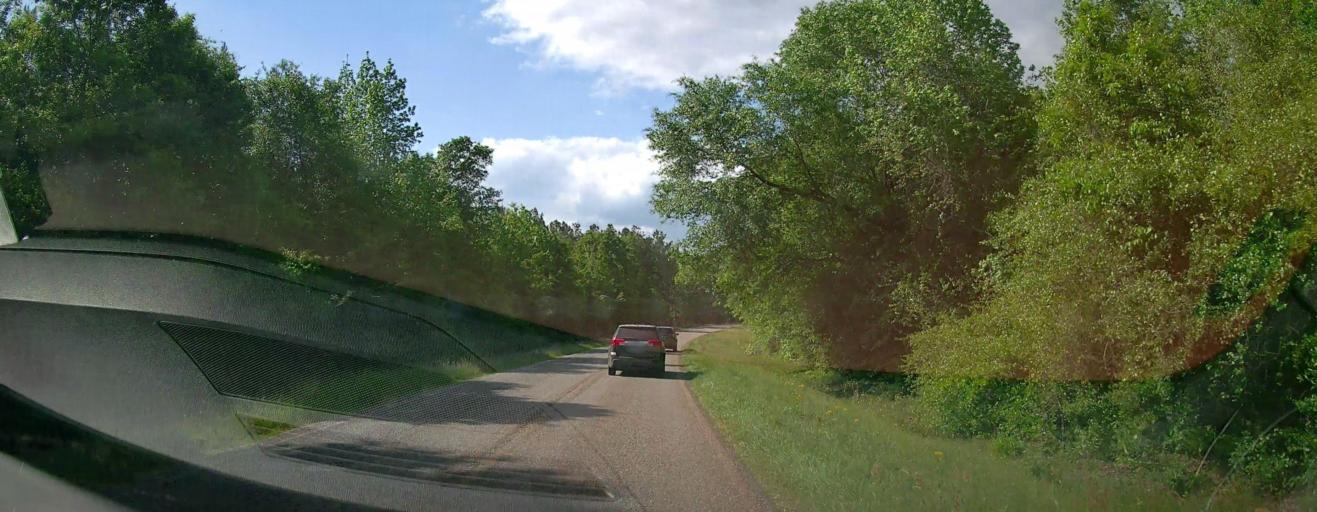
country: US
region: Georgia
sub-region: Laurens County
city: East Dublin
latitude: 32.7043
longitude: -82.9172
